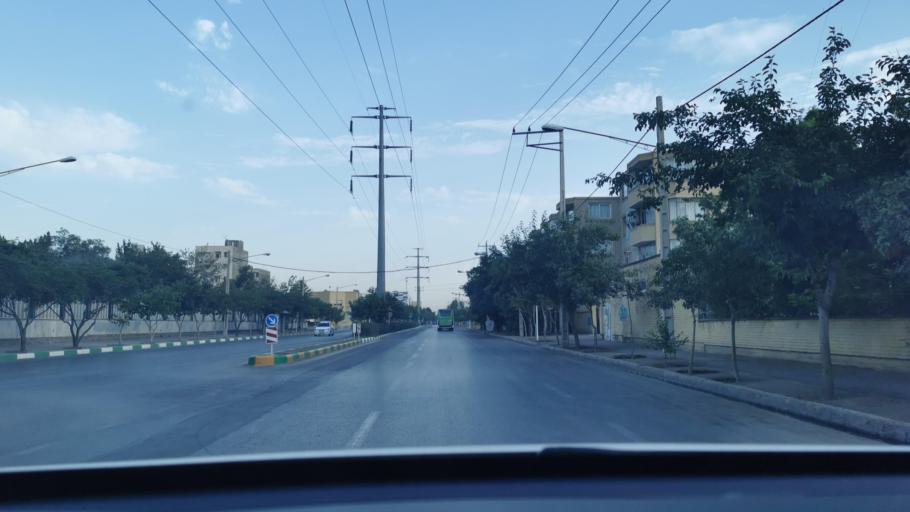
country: IR
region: Razavi Khorasan
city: Mashhad
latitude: 36.3532
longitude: 59.5285
